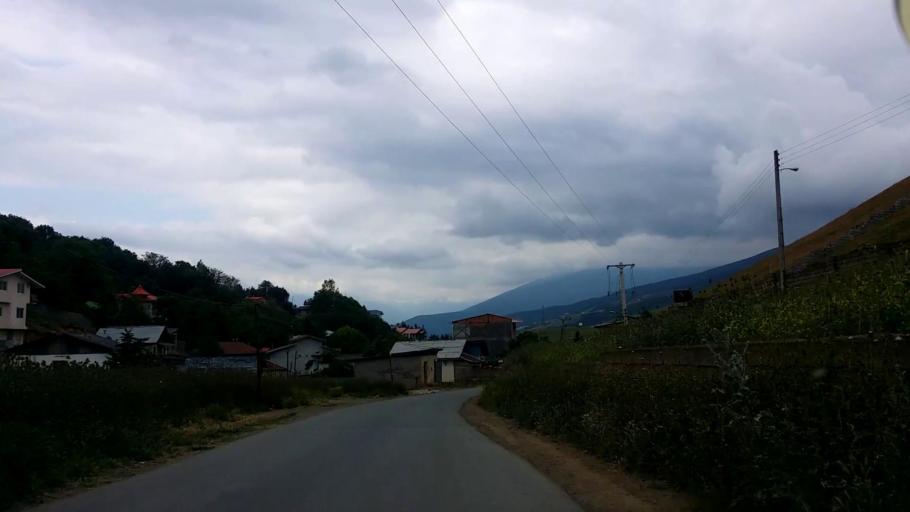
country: IR
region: Mazandaran
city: Chalus
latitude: 36.5175
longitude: 51.2596
